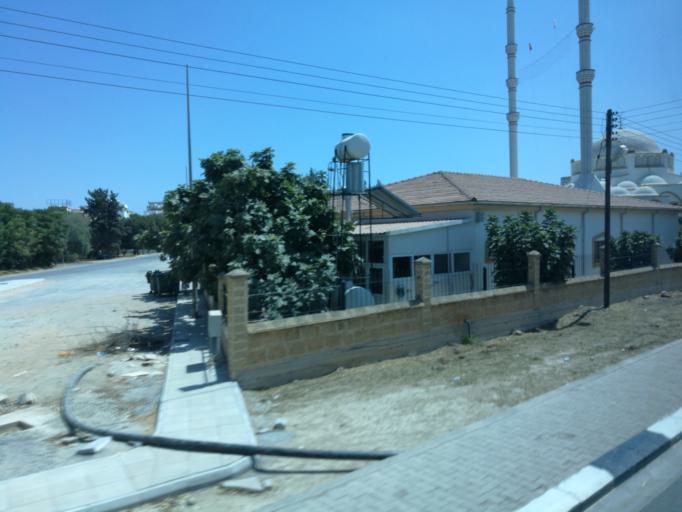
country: CY
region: Ammochostos
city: Famagusta
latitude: 35.1306
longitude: 33.9271
